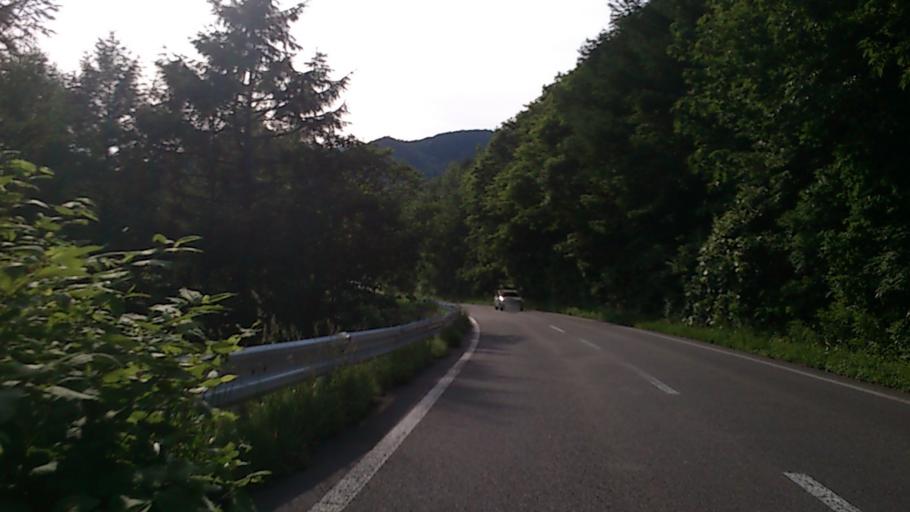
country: JP
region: Aomori
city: Aomori Shi
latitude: 40.6505
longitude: 140.7734
